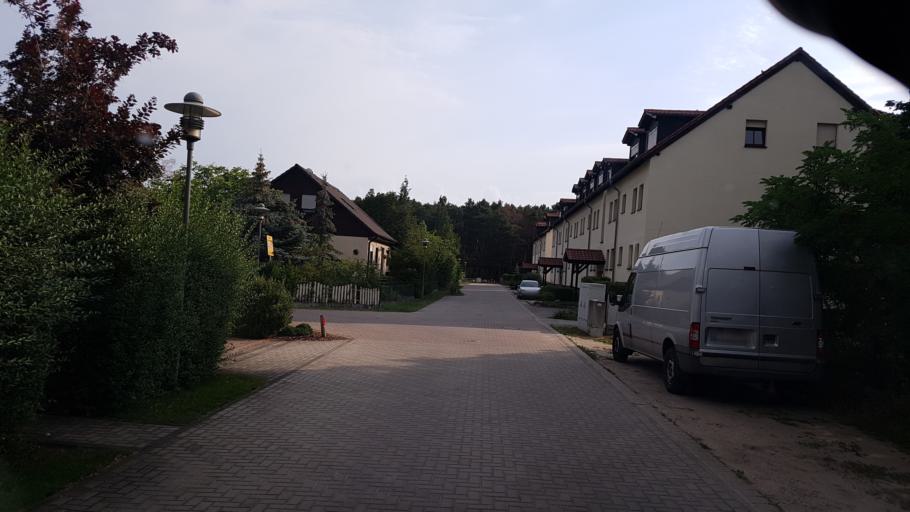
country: DE
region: Brandenburg
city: Baruth
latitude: 52.0402
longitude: 13.5157
